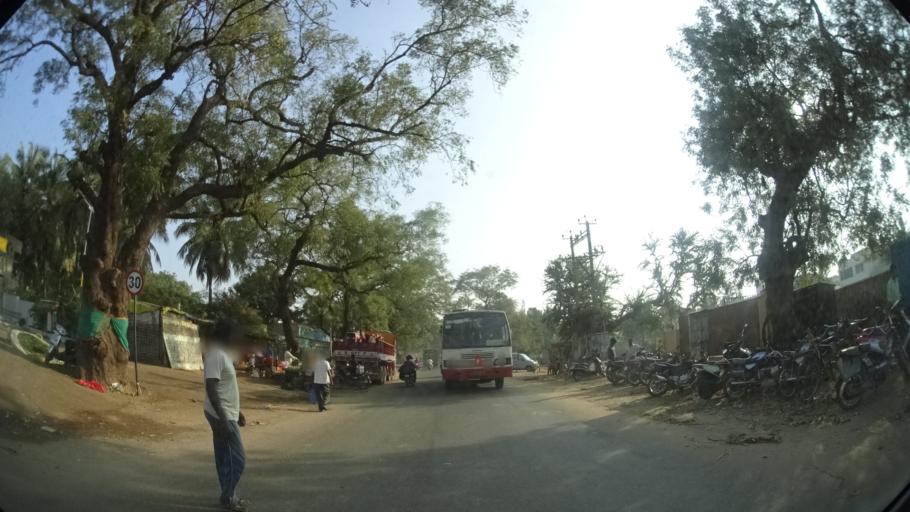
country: IN
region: Karnataka
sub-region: Bellary
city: Hospet
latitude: 15.2617
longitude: 76.3820
